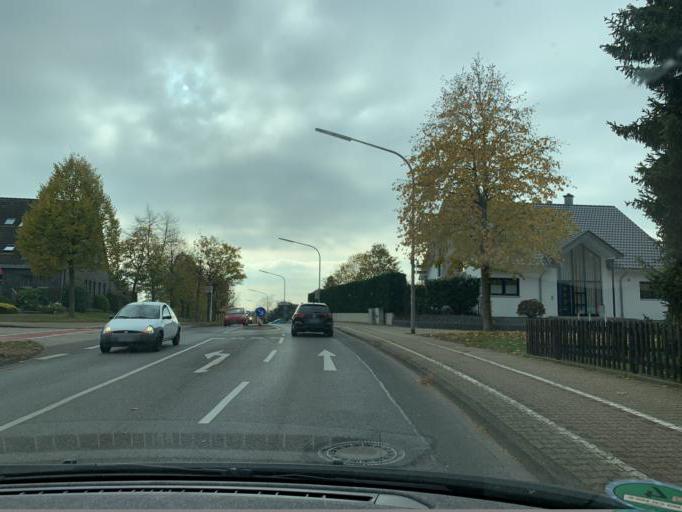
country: DE
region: North Rhine-Westphalia
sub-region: Regierungsbezirk Dusseldorf
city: Monchengladbach
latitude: 51.1526
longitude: 6.4396
